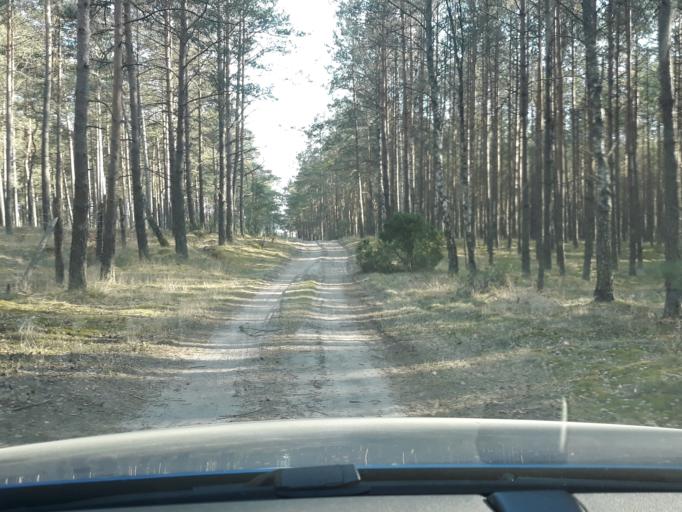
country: PL
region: Pomeranian Voivodeship
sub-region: Powiat bytowski
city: Lipnica
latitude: 53.8963
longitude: 17.4939
